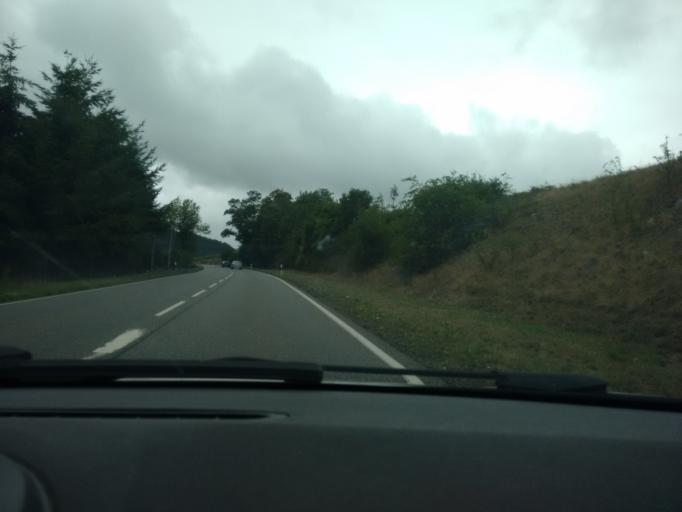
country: DE
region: Rheinland-Pfalz
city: Merxheim
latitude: 49.8026
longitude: 7.5586
